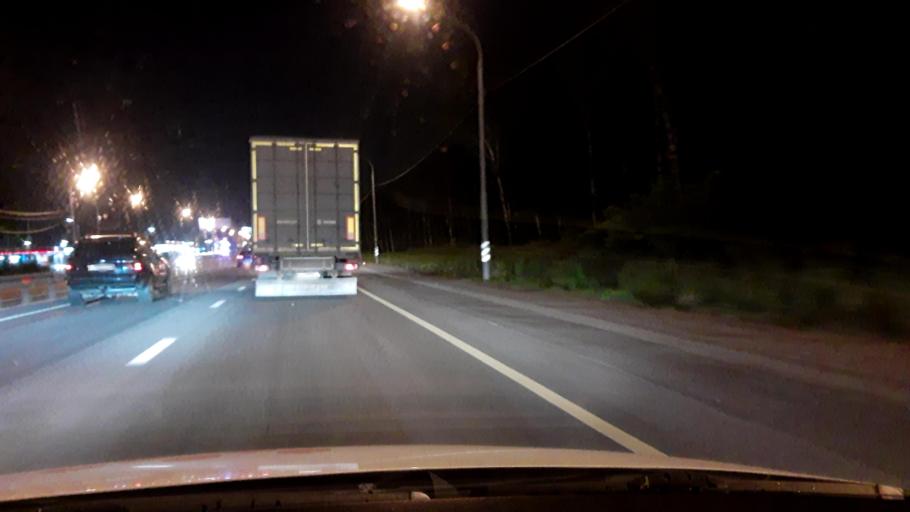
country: RU
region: Moskovskaya
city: Staraya Kupavna
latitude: 55.8219
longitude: 38.1800
